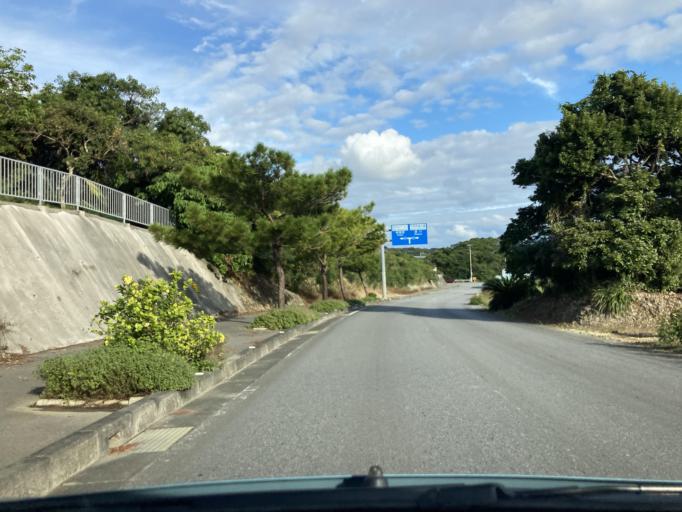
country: JP
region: Okinawa
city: Itoman
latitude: 26.1405
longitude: 127.7454
